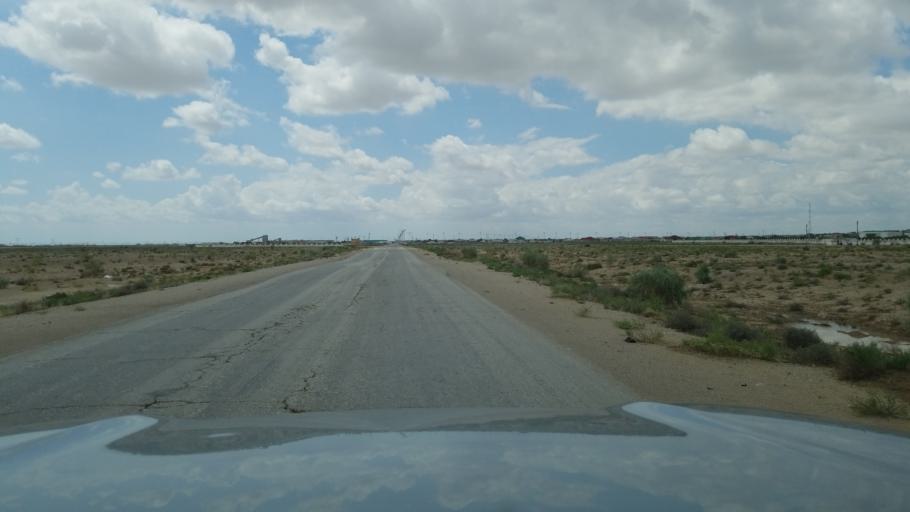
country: TM
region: Balkan
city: Balkanabat
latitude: 39.4890
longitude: 54.4034
